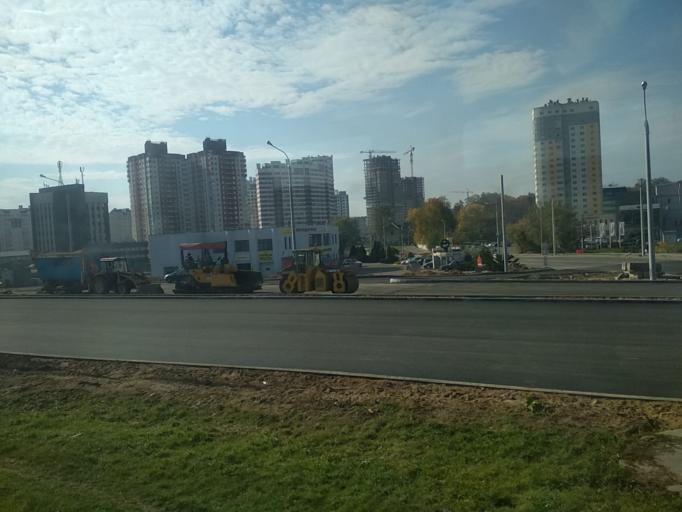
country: BY
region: Minsk
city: Minsk
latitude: 53.8731
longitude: 27.5620
